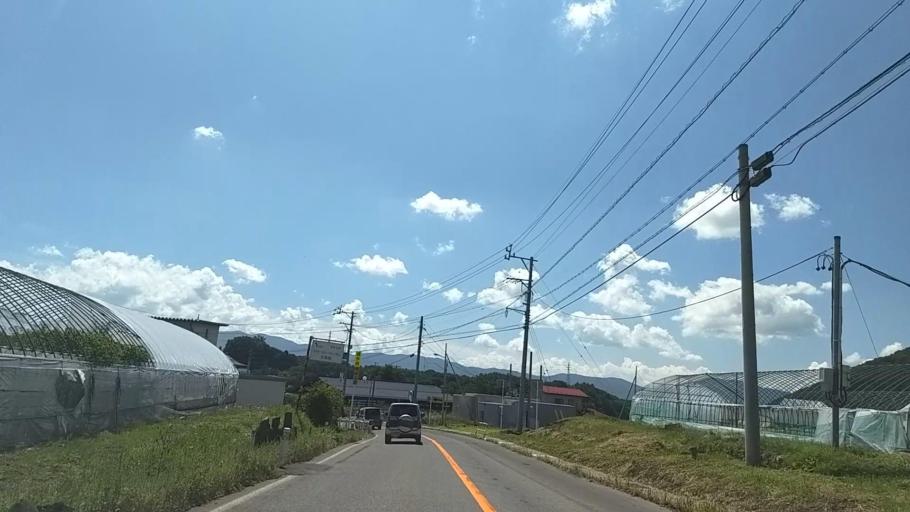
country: JP
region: Nagano
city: Chino
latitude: 36.0434
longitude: 138.2253
